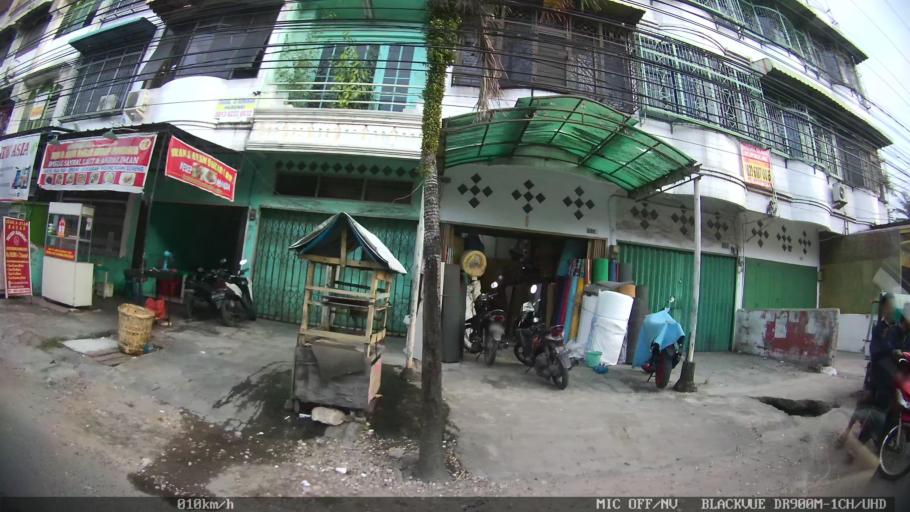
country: ID
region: North Sumatra
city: Medan
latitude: 3.5822
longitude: 98.7025
